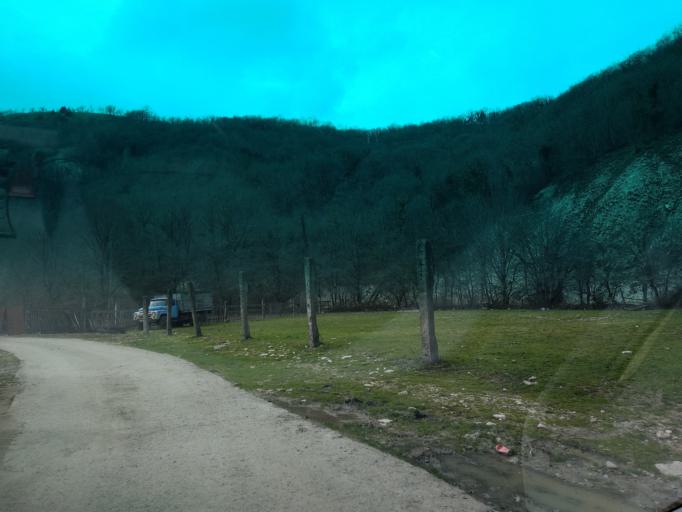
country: RU
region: Krasnodarskiy
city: Shepsi
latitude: 44.0672
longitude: 39.1409
